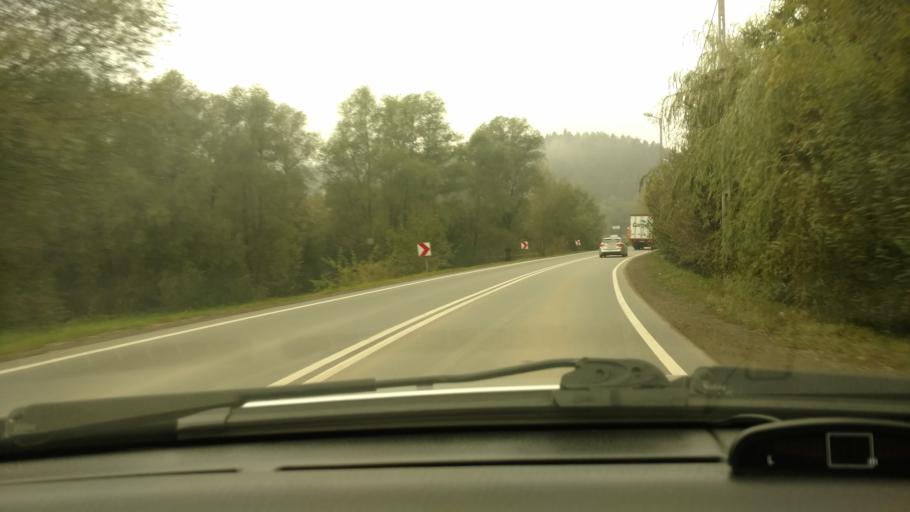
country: PL
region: Lesser Poland Voivodeship
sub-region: Powiat nowosadecki
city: Nawojowa
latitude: 49.6069
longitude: 20.7578
